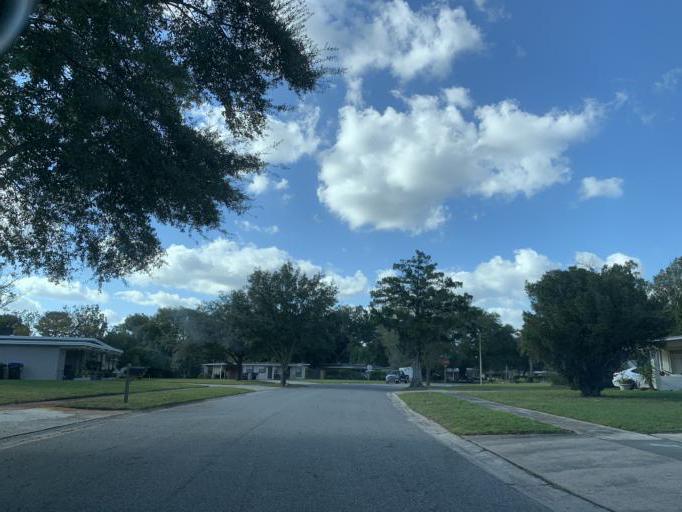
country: US
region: Florida
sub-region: Orange County
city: Fairview Shores
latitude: 28.6106
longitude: -81.4018
